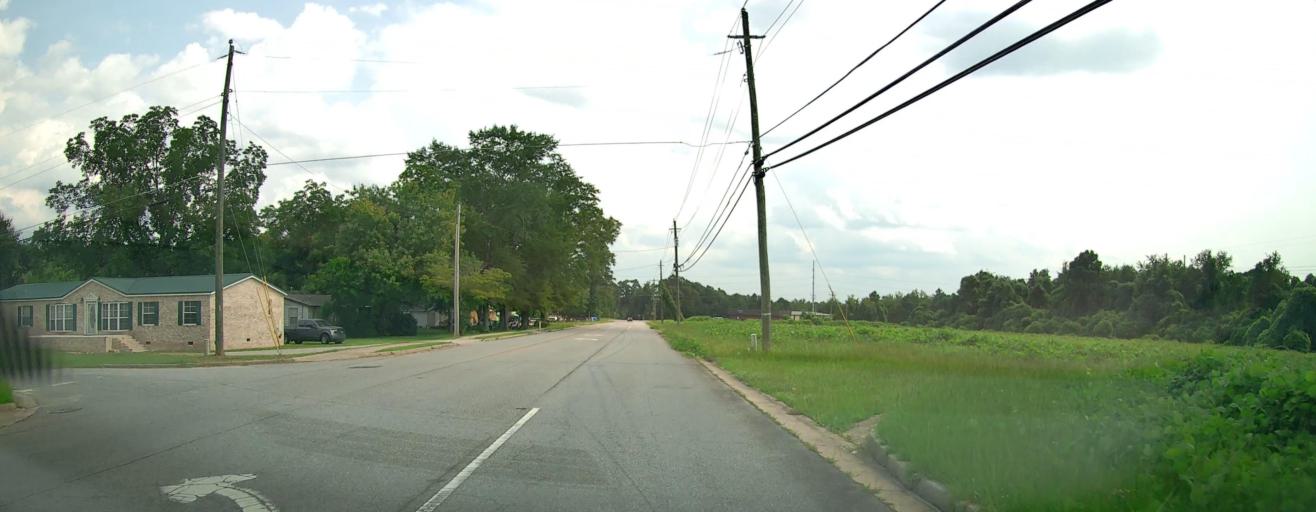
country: US
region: Georgia
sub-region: Houston County
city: Robins Air Force Base
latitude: 32.5924
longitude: -83.6034
